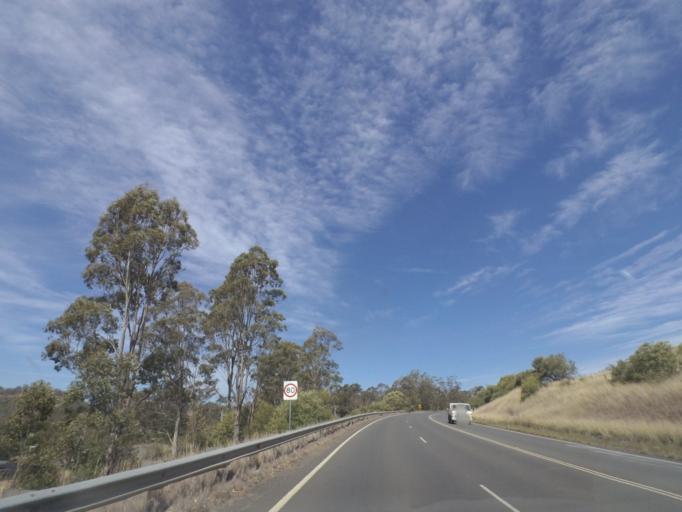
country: AU
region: New South Wales
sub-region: Wollondilly
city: Picton
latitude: -34.1634
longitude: 150.6202
